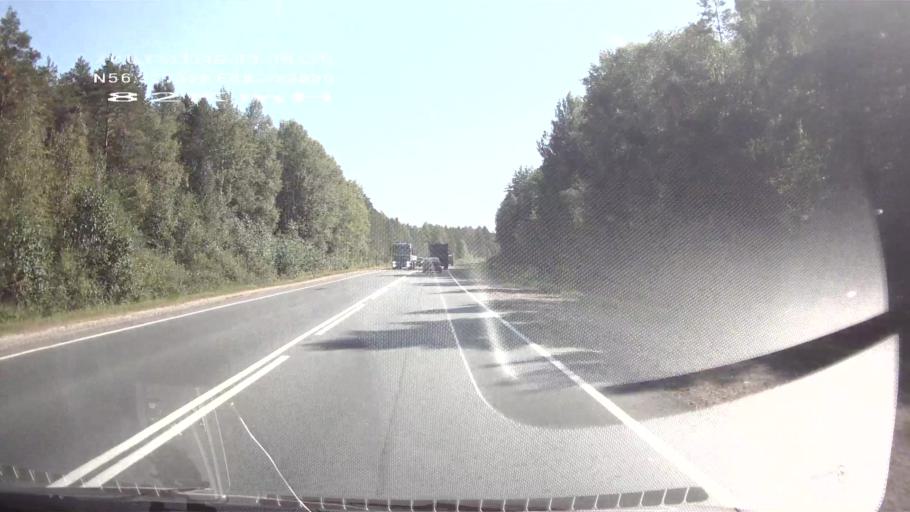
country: RU
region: Mariy-El
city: Suslonger
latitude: 56.3373
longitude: 48.2330
